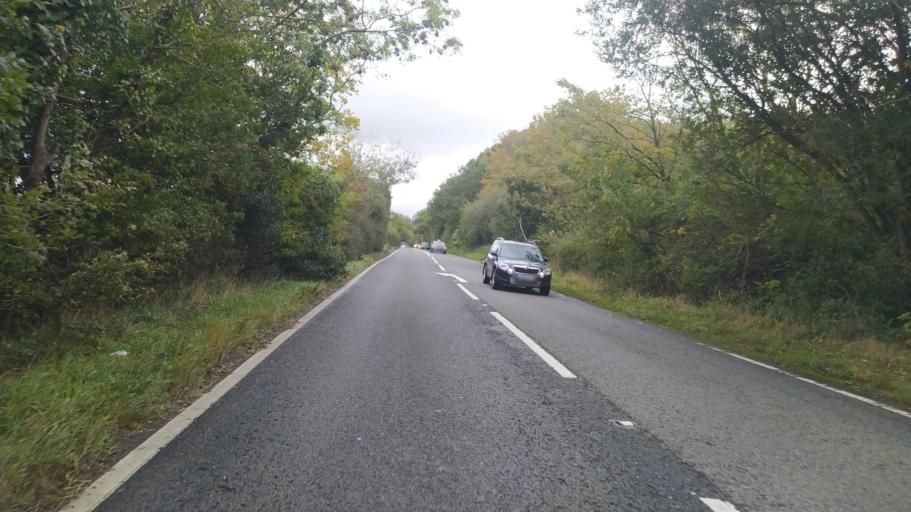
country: GB
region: England
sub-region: Dorset
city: Lyme Regis
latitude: 50.7411
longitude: -2.8791
